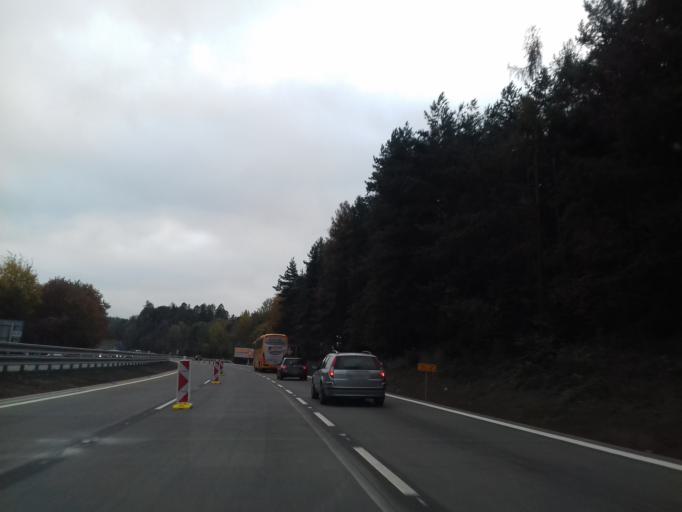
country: CZ
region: Central Bohemia
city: Ondrejov
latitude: 49.8472
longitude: 14.7972
